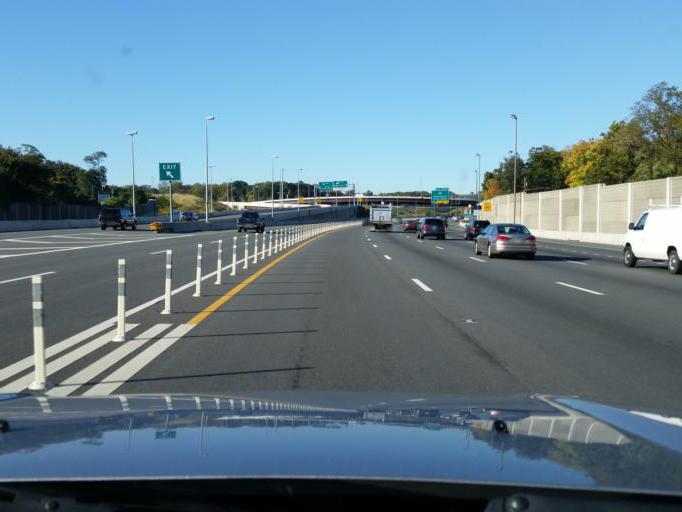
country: US
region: Virginia
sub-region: Fairfax County
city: Merrifield
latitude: 38.8794
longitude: -77.2211
